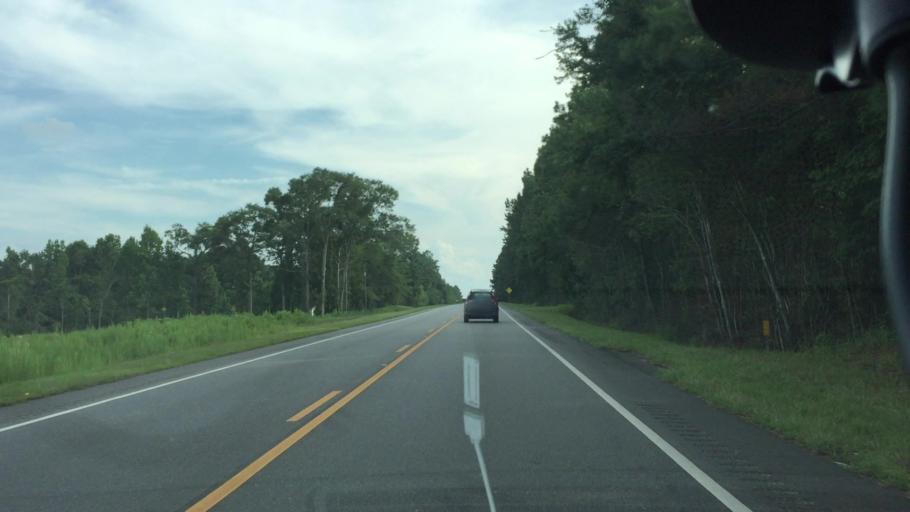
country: US
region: Alabama
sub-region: Pike County
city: Brundidge
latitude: 31.6083
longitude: -85.9466
